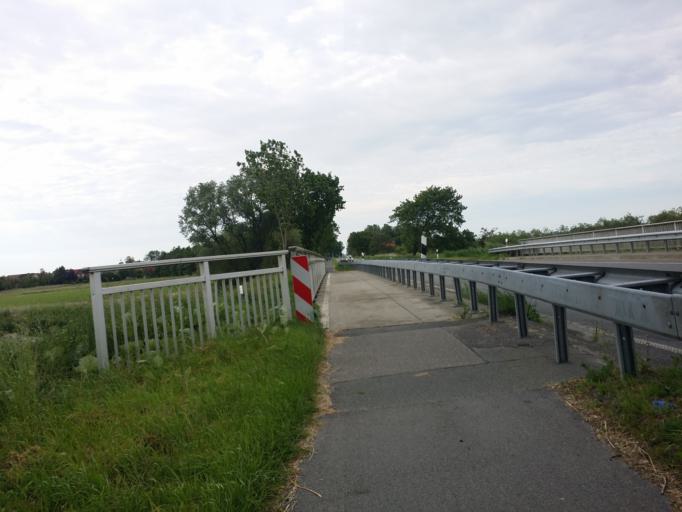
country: DE
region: Lower Saxony
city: Wittmund
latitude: 53.5914
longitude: 7.7859
